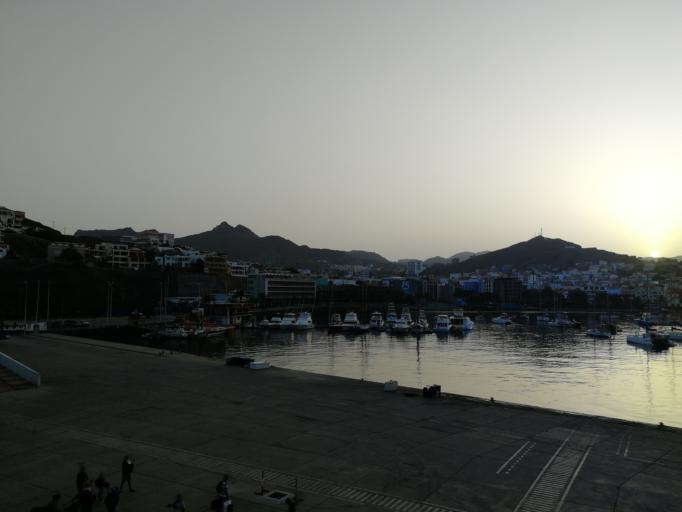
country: CV
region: Sao Vicente
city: Mindelo
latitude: 16.8874
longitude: -24.9935
